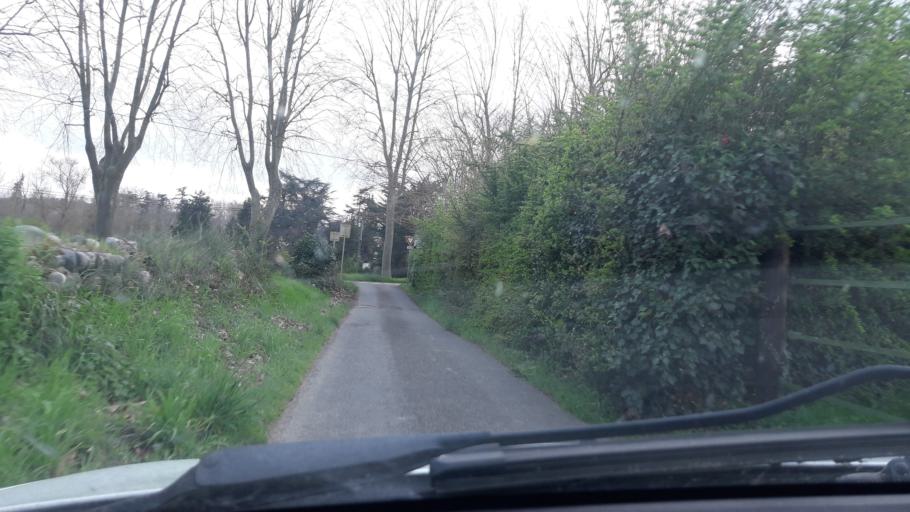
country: FR
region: Midi-Pyrenees
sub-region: Departement de la Haute-Garonne
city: Carbonne
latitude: 43.2926
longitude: 1.2196
